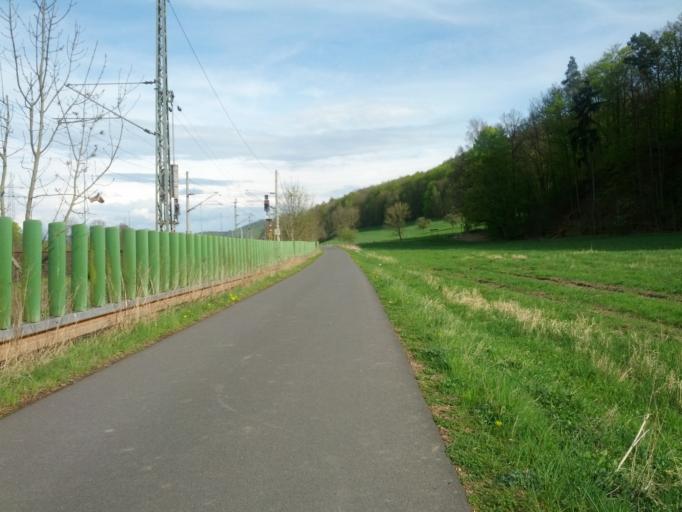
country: DE
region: Thuringia
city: Krauthausen
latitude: 50.9881
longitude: 10.2539
